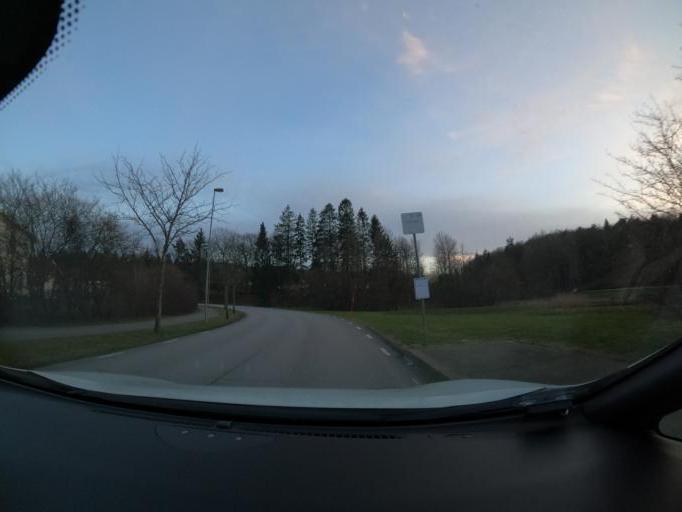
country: SE
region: Vaestra Goetaland
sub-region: Harryda Kommun
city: Molnlycke
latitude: 57.6437
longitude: 12.1062
